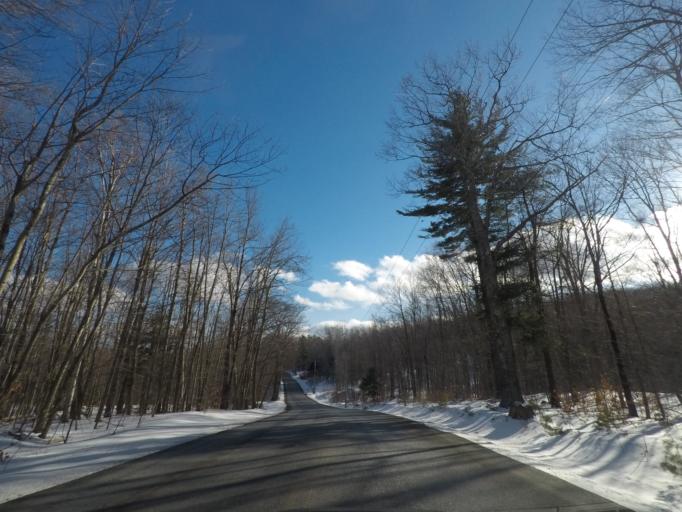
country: US
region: New York
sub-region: Rensselaer County
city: Hoosick Falls
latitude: 42.7940
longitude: -73.4015
